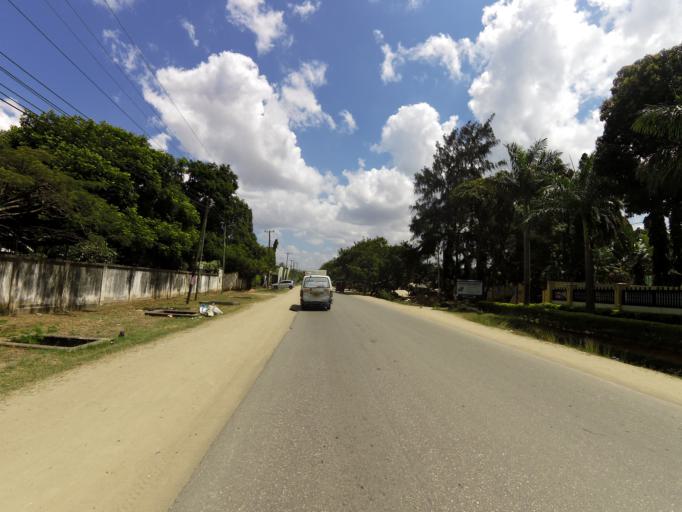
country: TZ
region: Dar es Salaam
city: Magomeni
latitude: -6.7624
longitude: 39.2505
